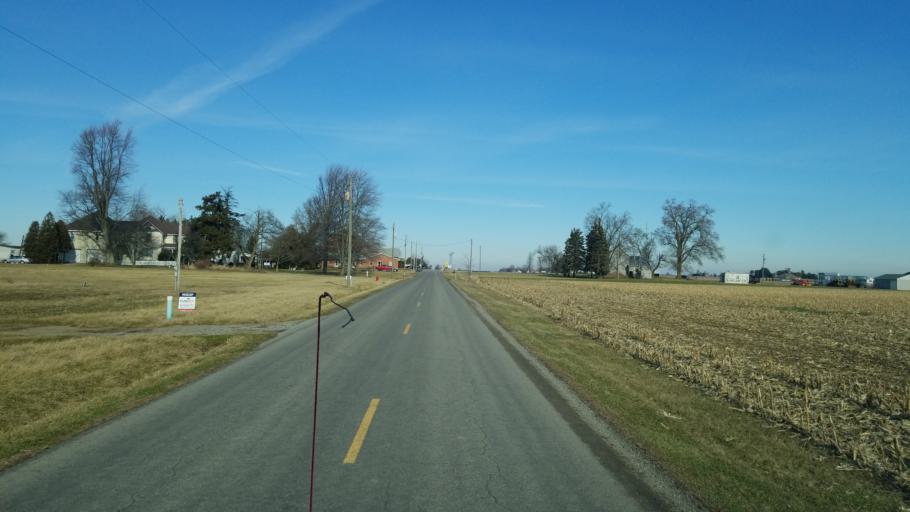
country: US
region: Ohio
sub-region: Putnam County
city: Pandora
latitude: 40.9460
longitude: -83.9380
